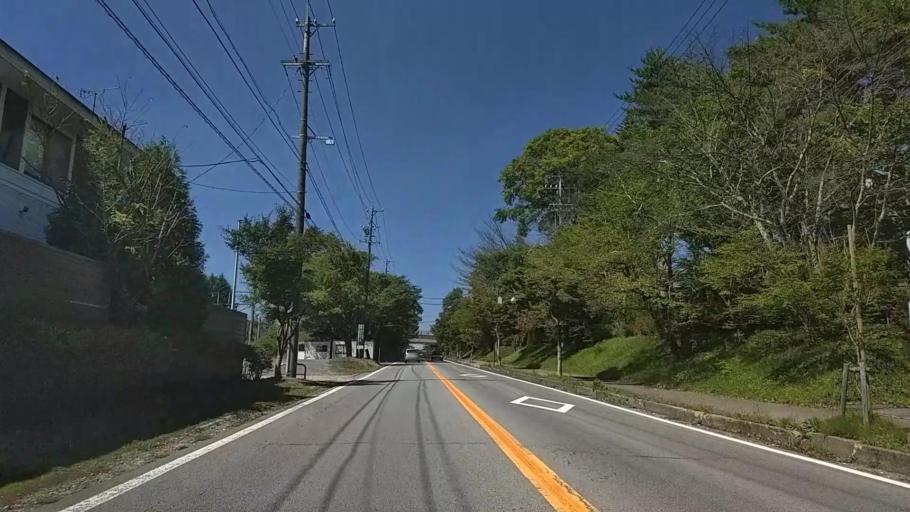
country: JP
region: Nagano
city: Saku
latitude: 36.3435
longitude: 138.6242
